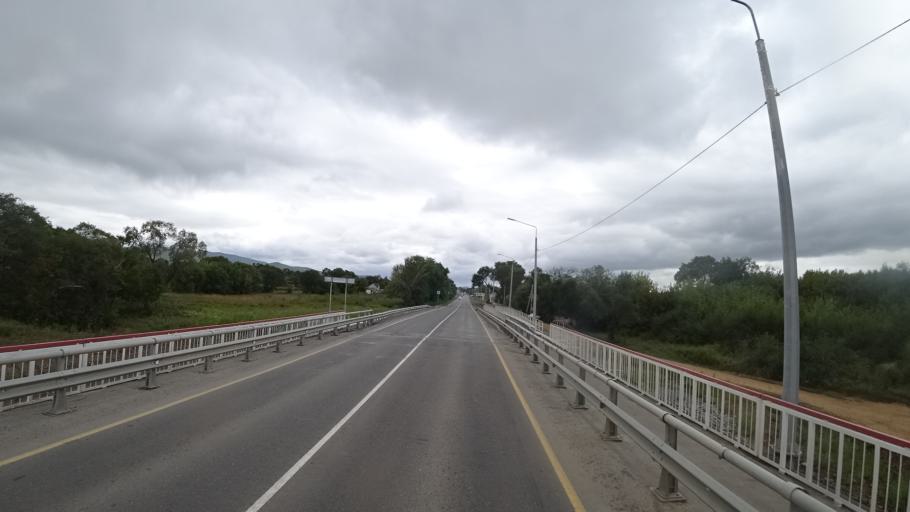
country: RU
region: Primorskiy
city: Chernigovka
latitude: 44.3423
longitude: 132.5903
